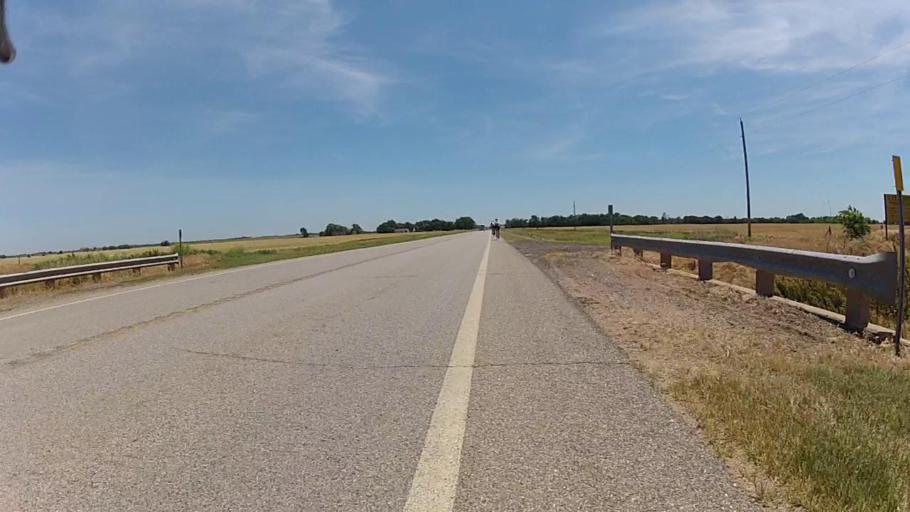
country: US
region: Kansas
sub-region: Barber County
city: Medicine Lodge
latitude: 37.2534
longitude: -98.4403
